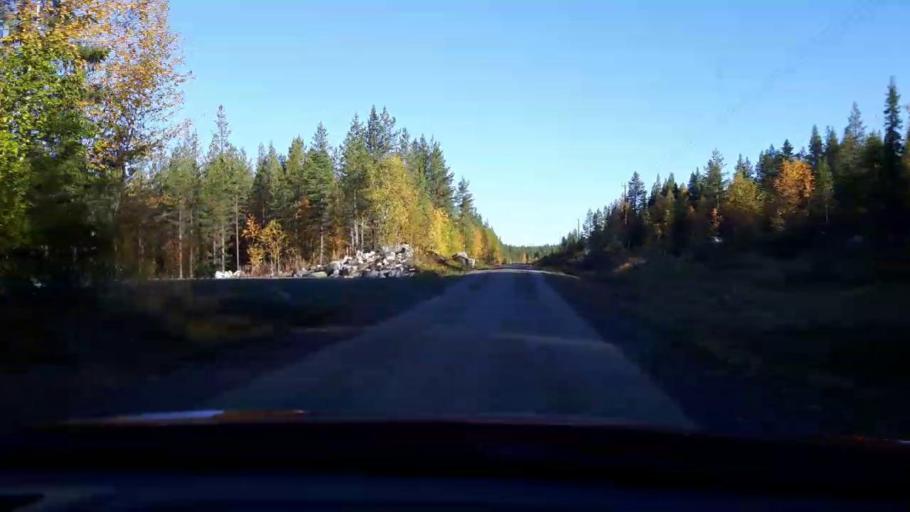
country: SE
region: Jaemtland
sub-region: Stroemsunds Kommun
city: Stroemsund
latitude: 64.3751
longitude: 15.1511
